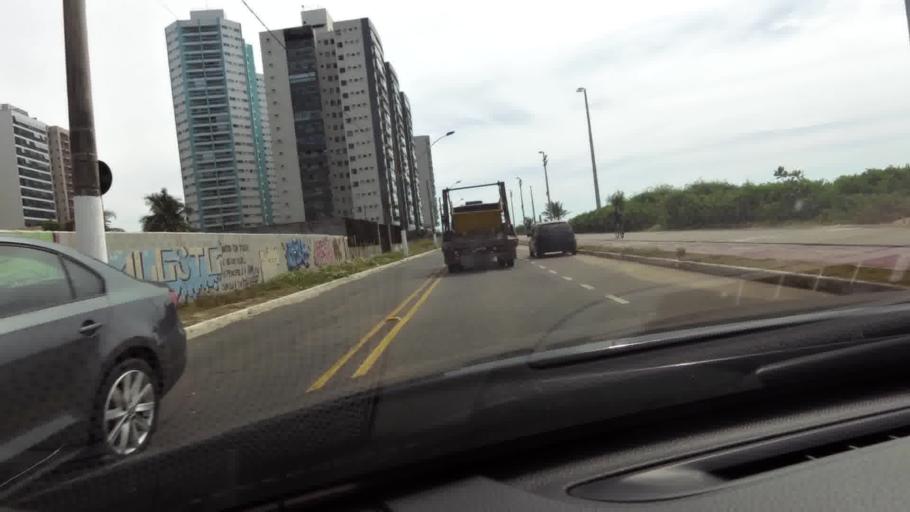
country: BR
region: Espirito Santo
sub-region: Vila Velha
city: Vila Velha
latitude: -20.3797
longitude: -40.3078
